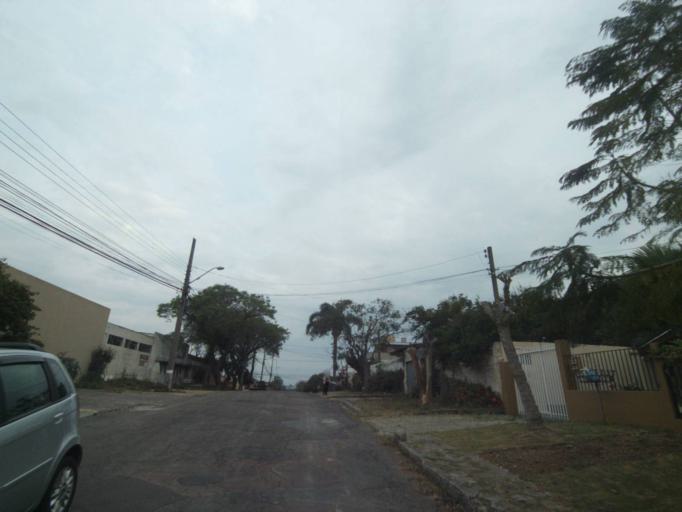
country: BR
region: Parana
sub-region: Pinhais
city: Pinhais
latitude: -25.4708
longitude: -49.2322
